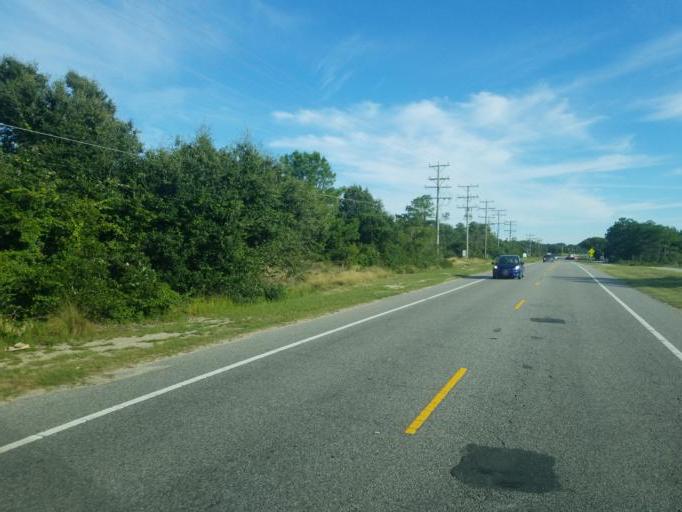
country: US
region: North Carolina
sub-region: Dare County
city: Southern Shores
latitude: 36.3221
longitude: -75.8159
